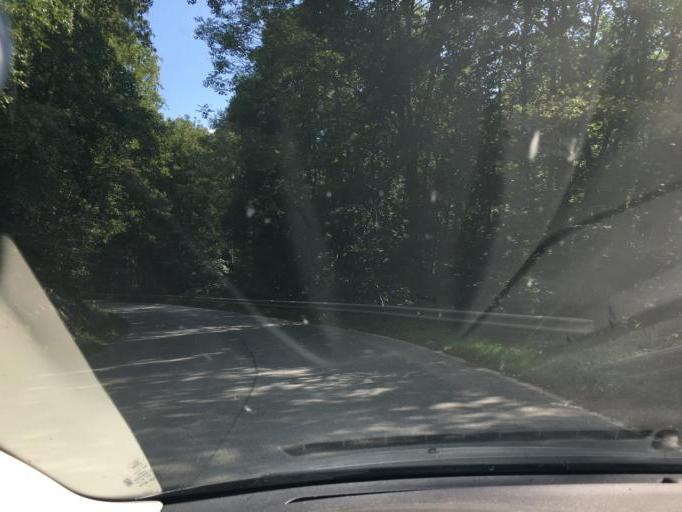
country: CZ
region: Liberecky
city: Zelezny Brod
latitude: 50.6095
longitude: 15.2778
